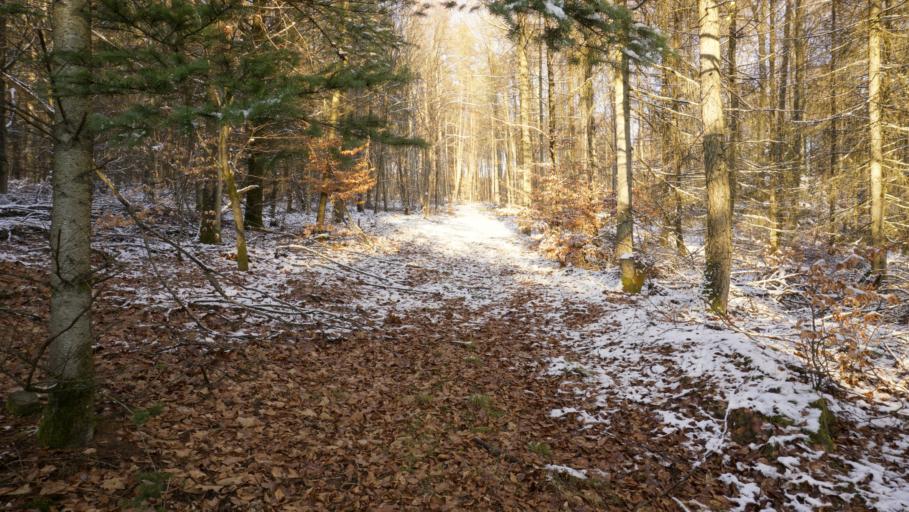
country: DE
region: Baden-Wuerttemberg
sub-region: Karlsruhe Region
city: Fahrenbach
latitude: 49.4238
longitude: 9.1065
